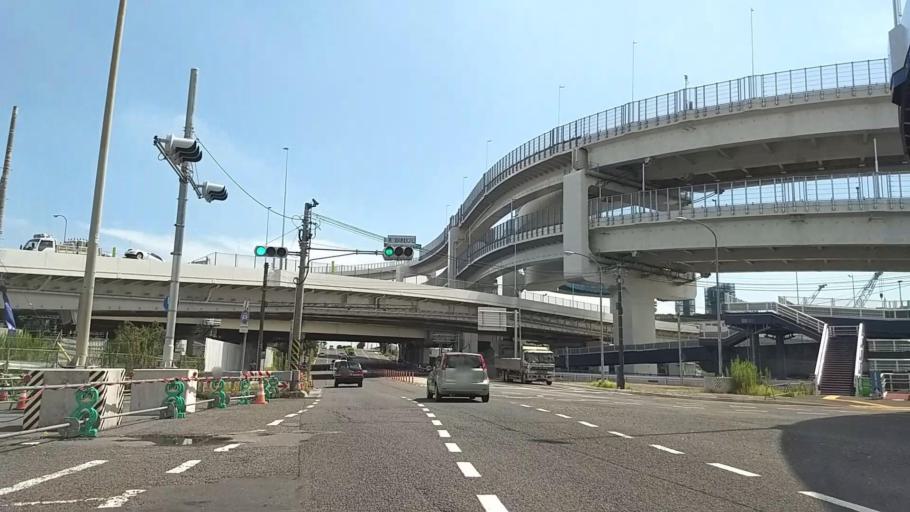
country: JP
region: Kanagawa
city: Yokohama
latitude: 35.5186
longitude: 139.5919
